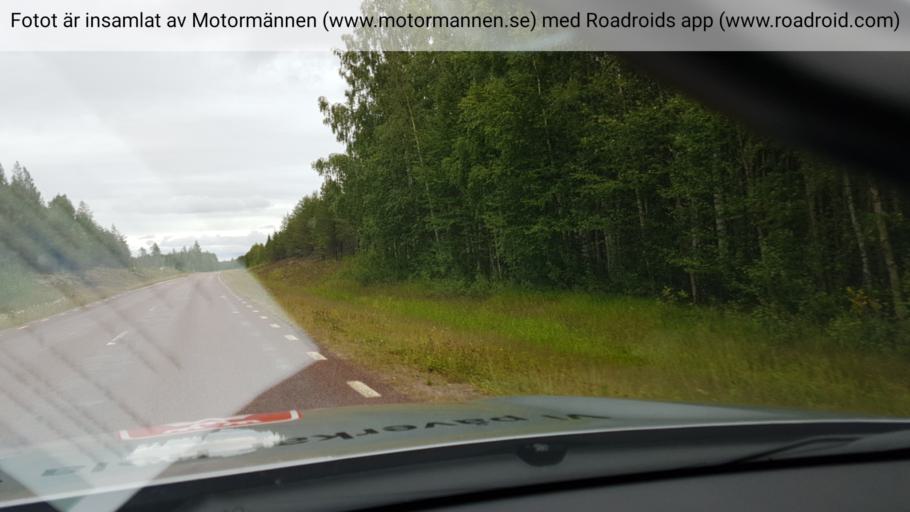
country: SE
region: Norrbotten
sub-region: Pajala Kommun
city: Pajala
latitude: 67.1401
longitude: 22.6144
